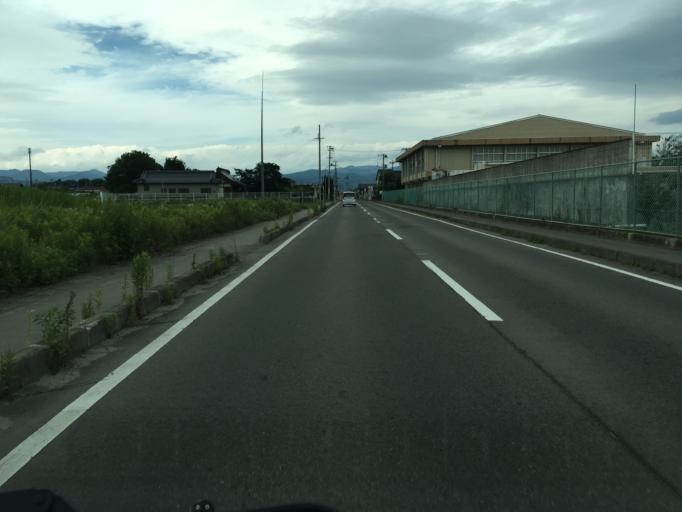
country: JP
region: Fukushima
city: Fukushima-shi
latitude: 37.7721
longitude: 140.4346
